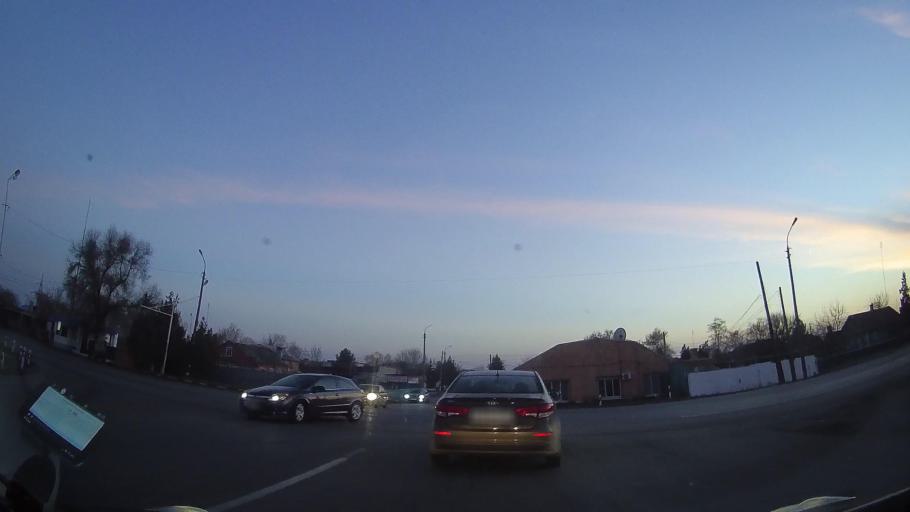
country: RU
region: Rostov
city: Zernograd
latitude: 46.8117
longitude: 40.2995
